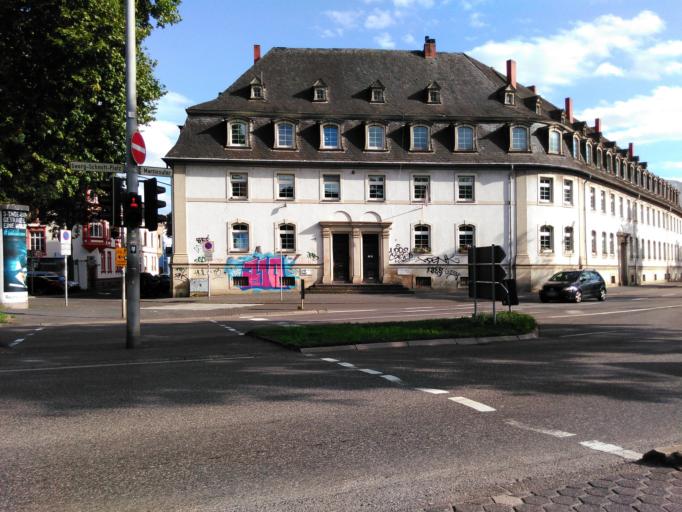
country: DE
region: Rheinland-Pfalz
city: Trier
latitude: 49.7636
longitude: 6.6339
